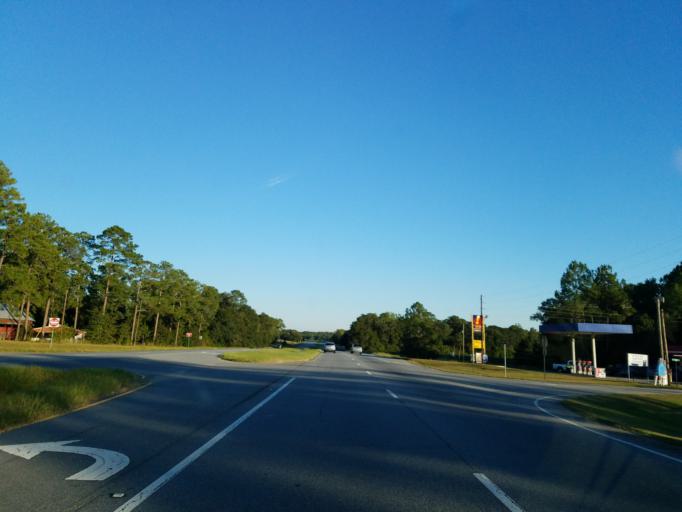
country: US
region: Georgia
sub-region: Worth County
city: Sylvester
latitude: 31.5180
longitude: -83.7850
